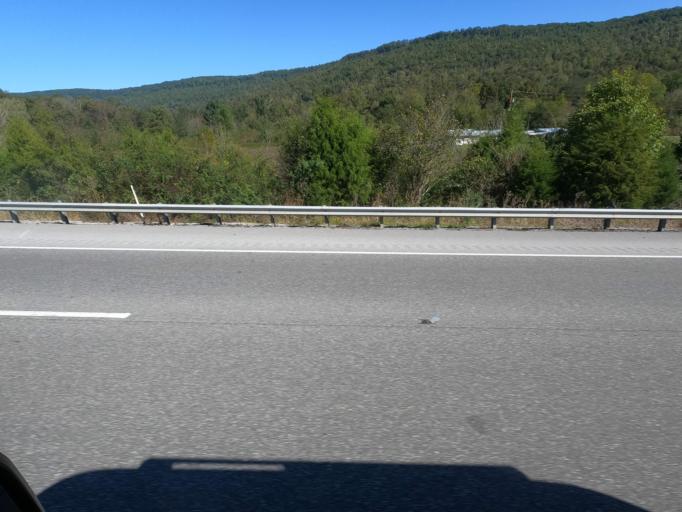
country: US
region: Tennessee
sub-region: Marion County
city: Monteagle
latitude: 35.1726
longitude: -85.7929
